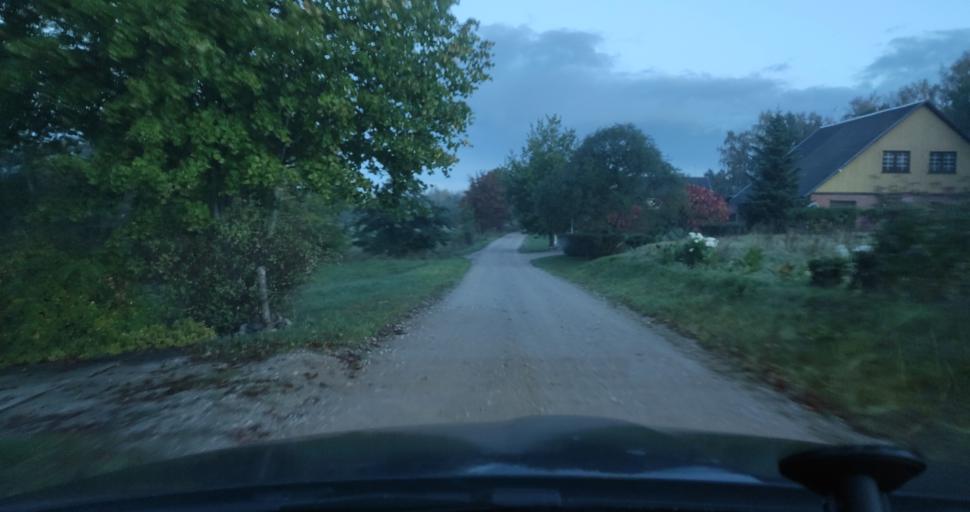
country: LV
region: Kuldigas Rajons
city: Kuldiga
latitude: 56.8837
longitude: 21.8191
